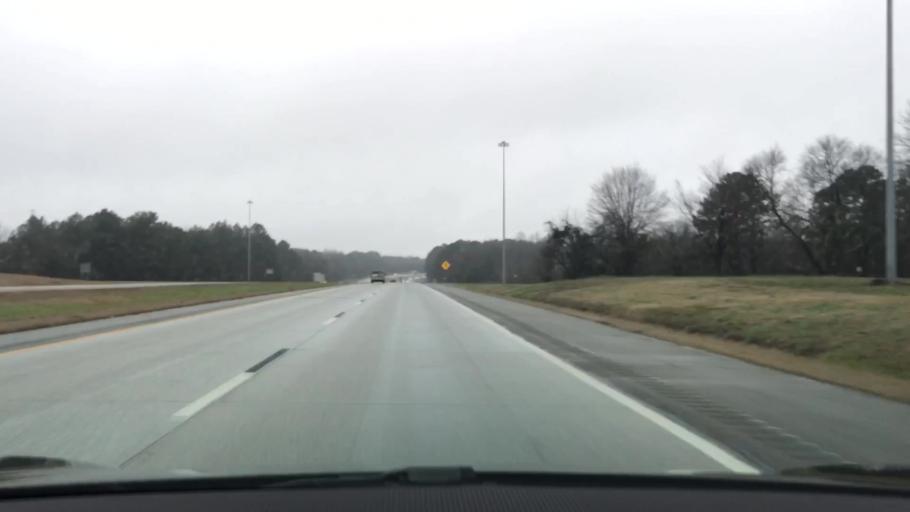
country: US
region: Georgia
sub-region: Morgan County
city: Madison
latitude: 33.5554
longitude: -83.4764
